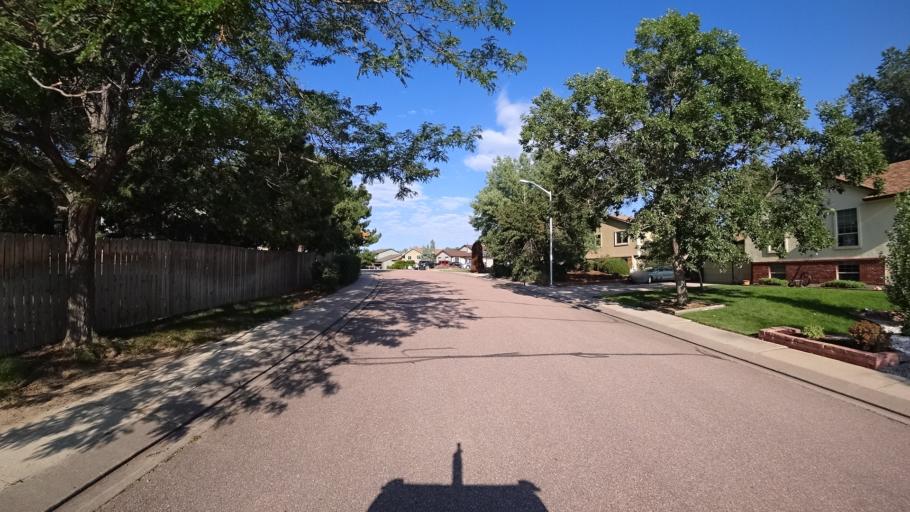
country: US
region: Colorado
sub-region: El Paso County
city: Black Forest
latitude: 38.9461
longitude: -104.7705
